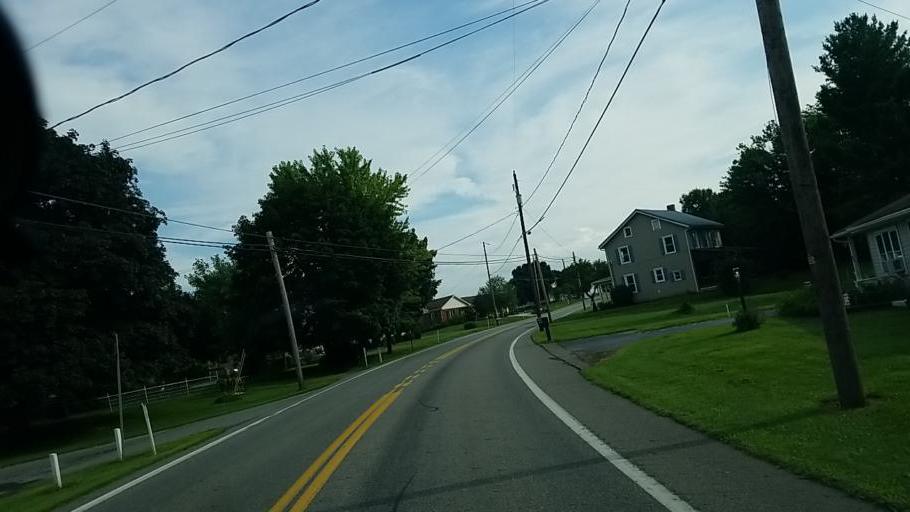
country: US
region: Pennsylvania
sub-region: Dauphin County
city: Millersburg
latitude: 40.5631
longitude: -76.9232
